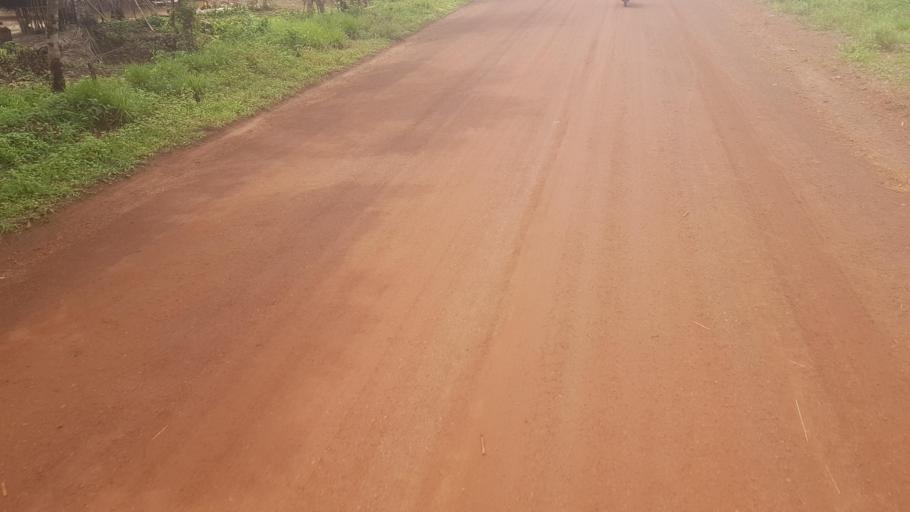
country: SL
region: Southern Province
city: Mogbwemo
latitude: 7.7511
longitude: -12.3075
